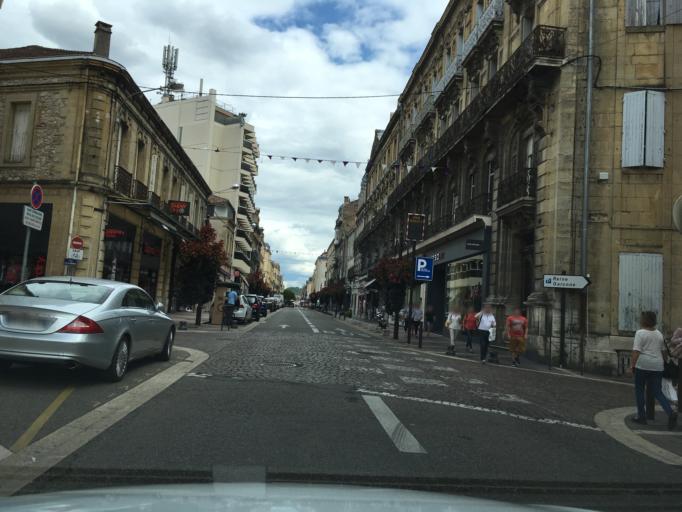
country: FR
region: Aquitaine
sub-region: Departement du Lot-et-Garonne
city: Le Passage
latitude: 44.2045
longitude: 0.6149
